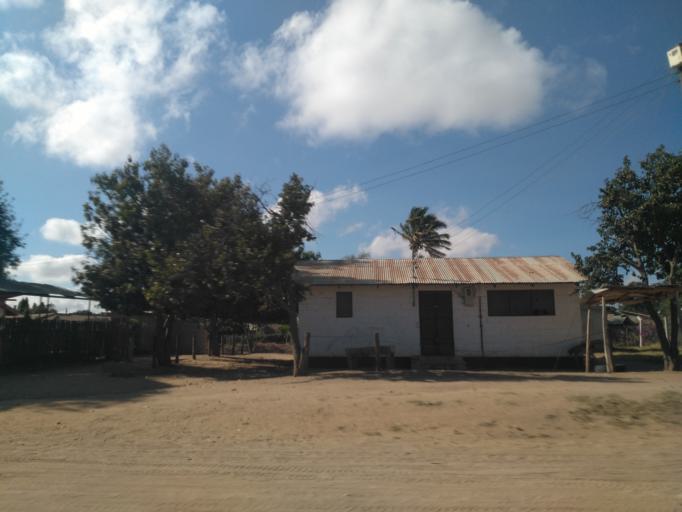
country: TZ
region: Dodoma
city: Dodoma
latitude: -6.1871
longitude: 35.7351
